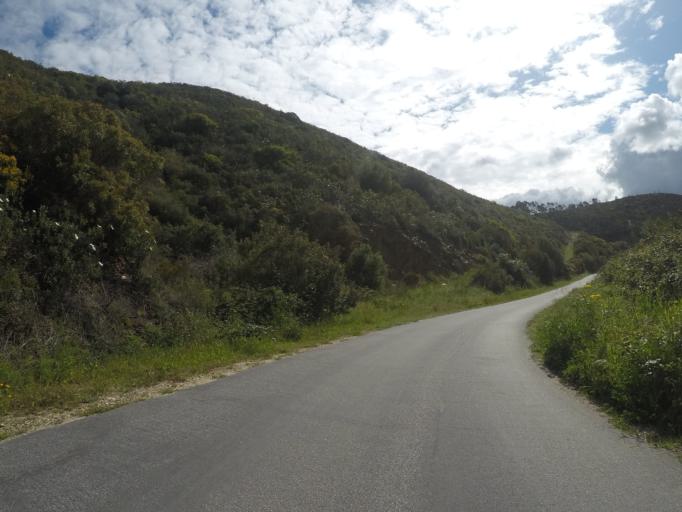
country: PT
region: Beja
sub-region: Odemira
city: Sao Teotonio
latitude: 37.4386
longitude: -8.7899
